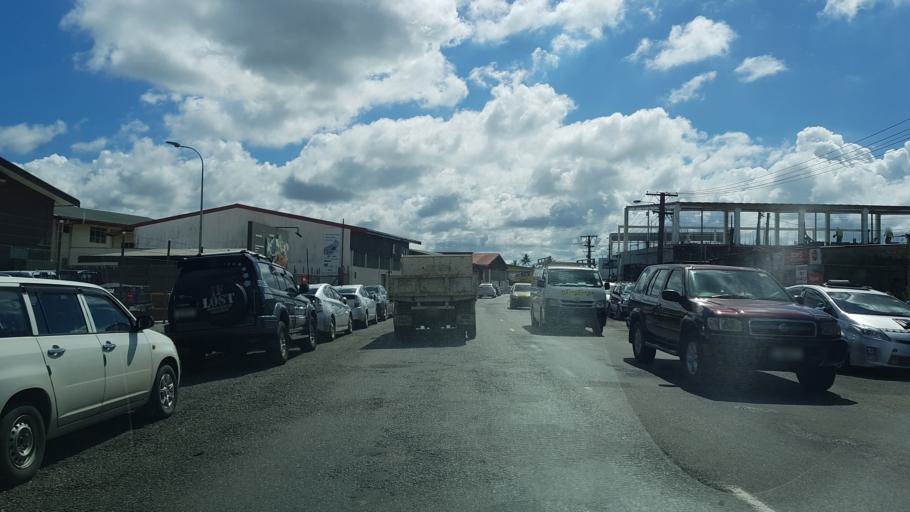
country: FJ
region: Central
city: Suva
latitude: -18.1275
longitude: 178.4561
